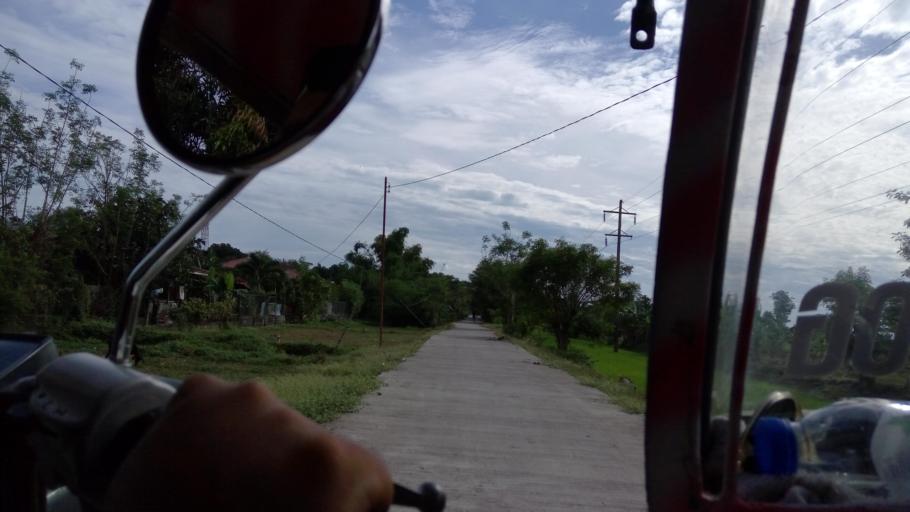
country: PH
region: Ilocos
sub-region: Province of La Union
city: San Eugenio
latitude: 16.3640
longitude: 120.3525
